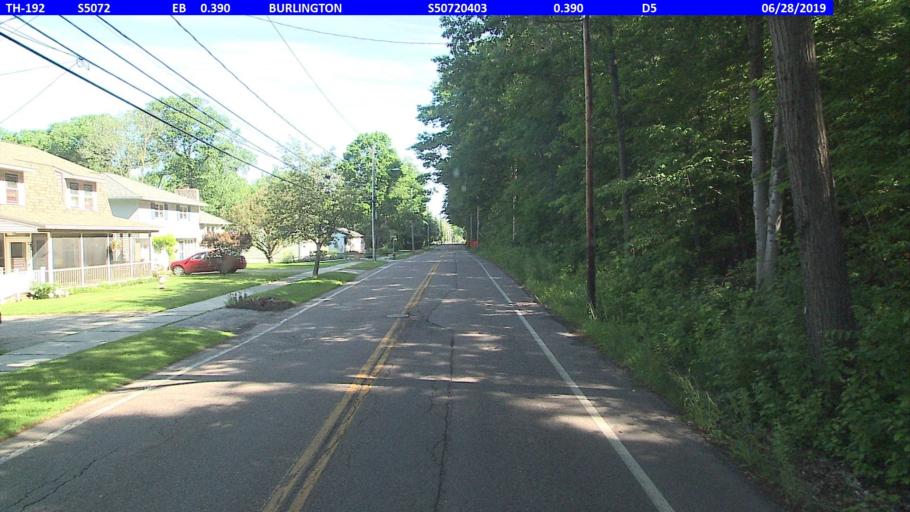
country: US
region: Vermont
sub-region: Chittenden County
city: Burlington
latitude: 44.5093
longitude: -73.2415
